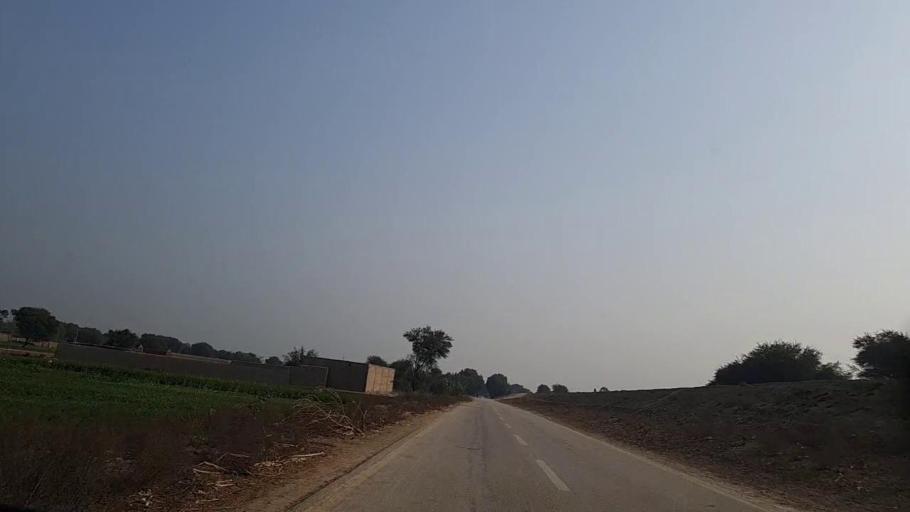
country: PK
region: Sindh
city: Sann
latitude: 26.1601
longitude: 68.1149
